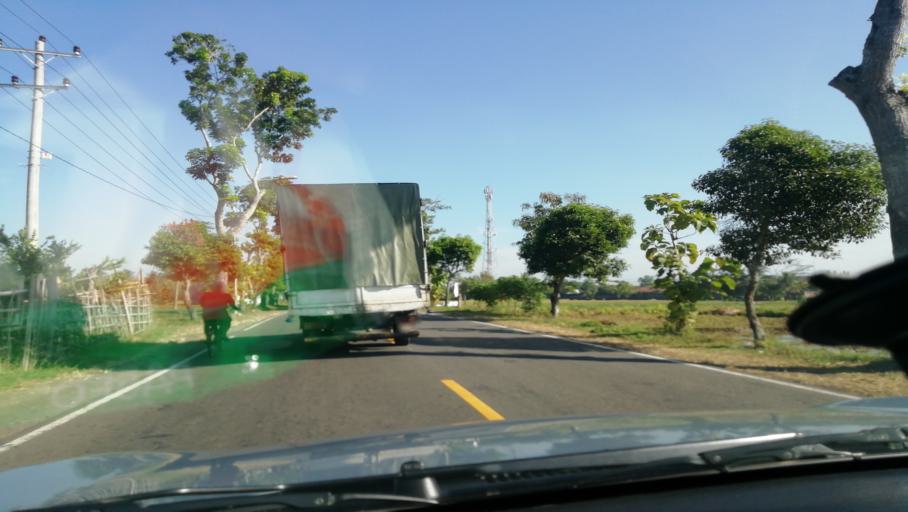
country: ID
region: Central Java
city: Kutoarjo
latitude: -7.7313
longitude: 109.9742
